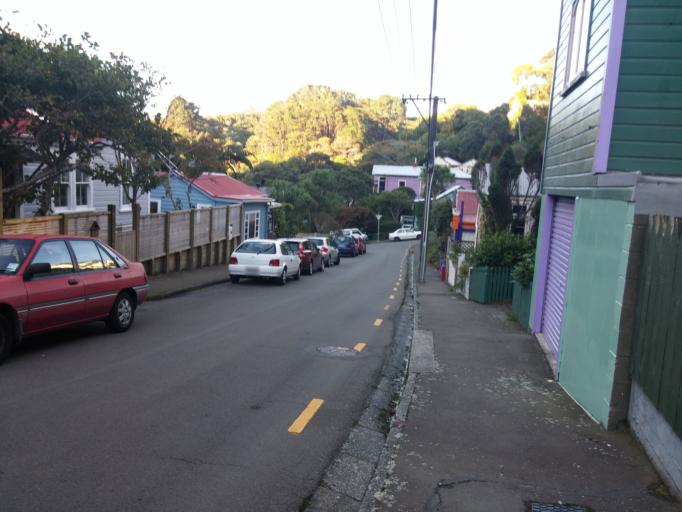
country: NZ
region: Wellington
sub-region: Wellington City
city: Kelburn
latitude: -41.2918
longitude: 174.7606
